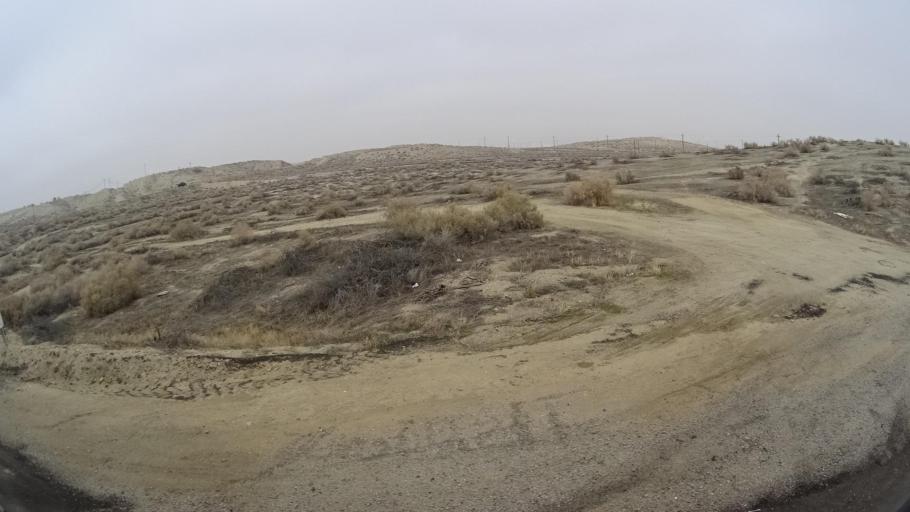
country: US
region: California
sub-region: Kern County
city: Maricopa
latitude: 35.0837
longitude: -119.4003
